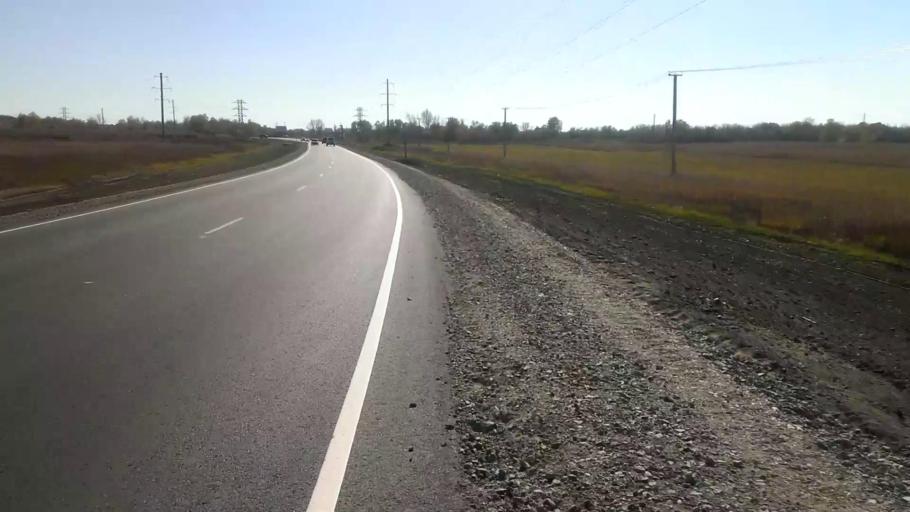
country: RU
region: Altai Krai
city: Sannikovo
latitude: 53.3330
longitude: 83.9379
